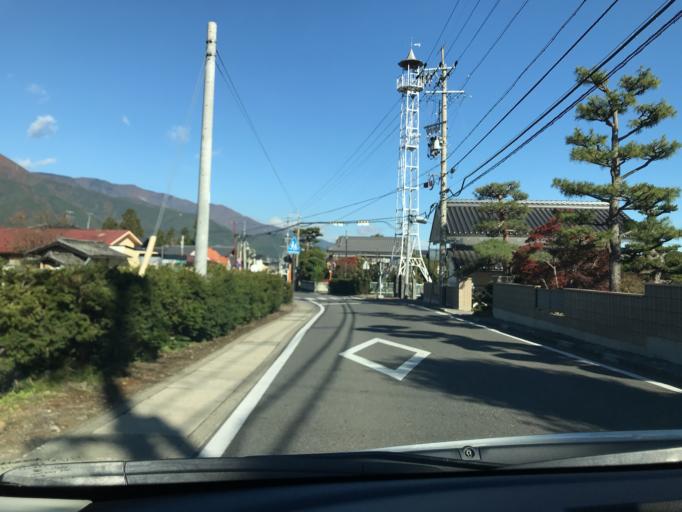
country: JP
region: Nagano
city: Toyoshina
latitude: 36.1903
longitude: 137.8551
